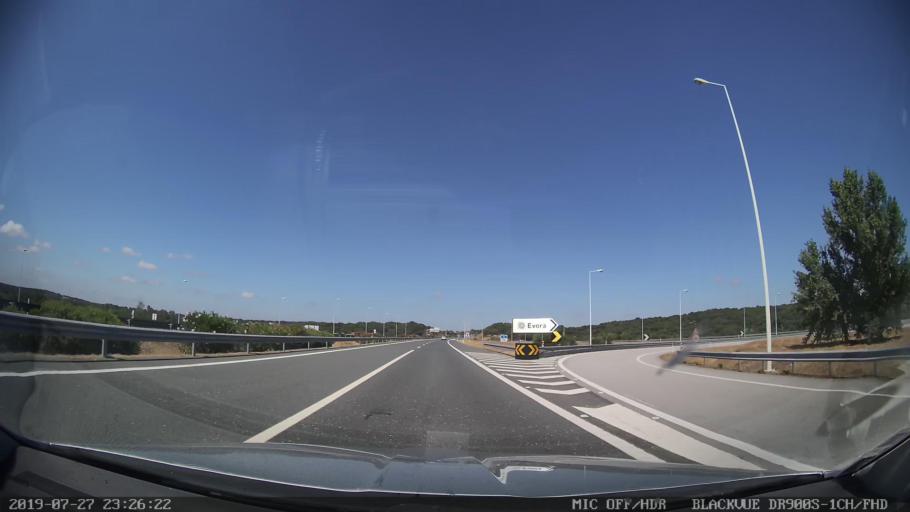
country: PT
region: Evora
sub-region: Arraiolos
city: Arraiolos
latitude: 38.6028
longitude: -8.0252
